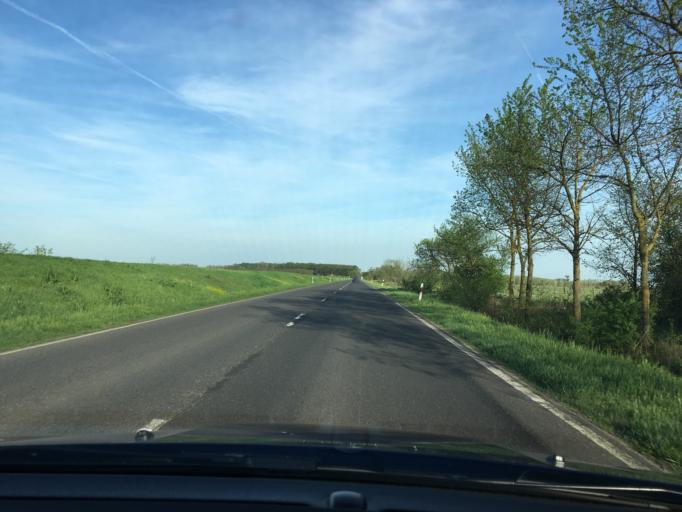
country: HU
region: Bekes
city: Szeghalom
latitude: 47.0073
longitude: 21.2030
